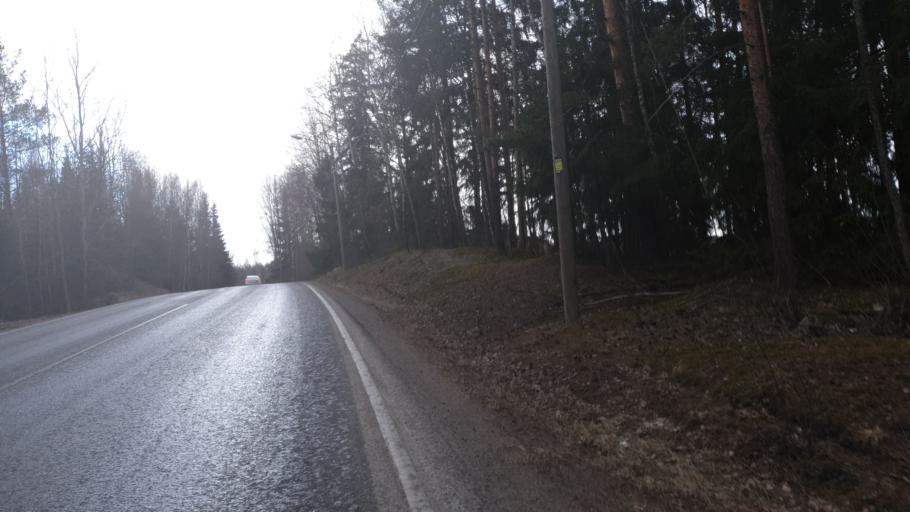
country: FI
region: Uusimaa
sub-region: Helsinki
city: Nurmijaervi
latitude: 60.3523
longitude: 24.7438
